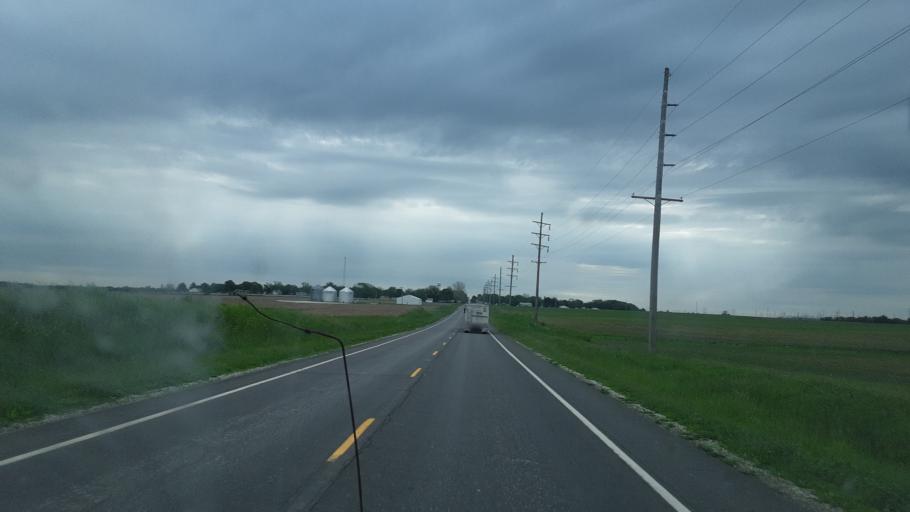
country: US
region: Illinois
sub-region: Fulton County
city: Astoria
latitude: 40.3516
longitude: -90.3427
